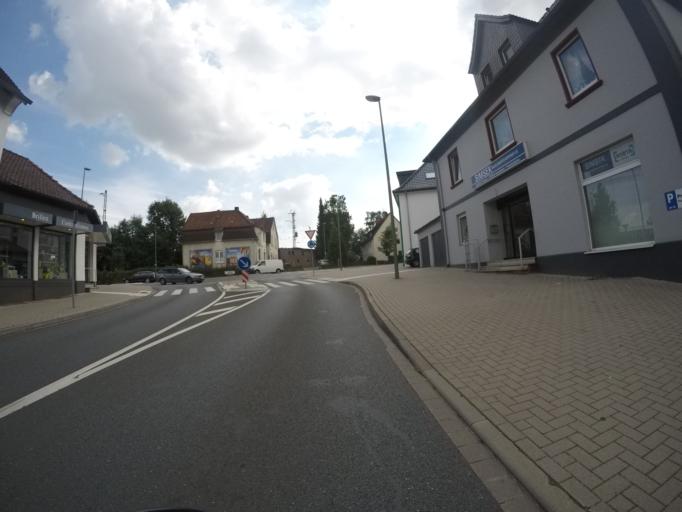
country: DE
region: North Rhine-Westphalia
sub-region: Regierungsbezirk Detmold
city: Herford
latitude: 52.0707
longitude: 8.6057
